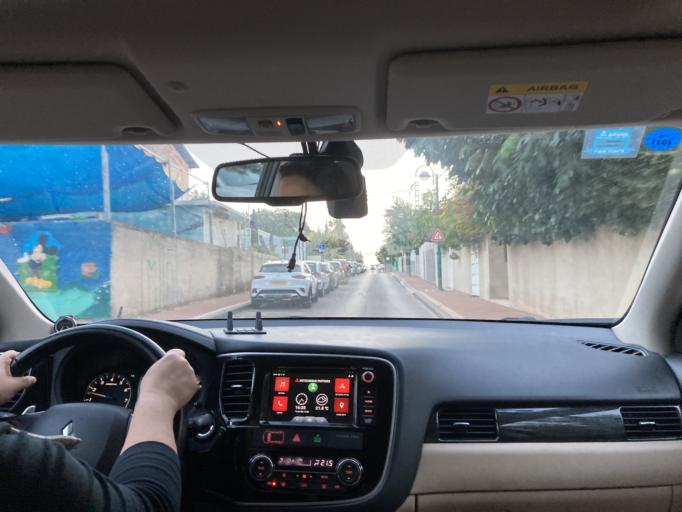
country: IL
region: Tel Aviv
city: Ramat HaSharon
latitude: 32.1510
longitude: 34.8379
